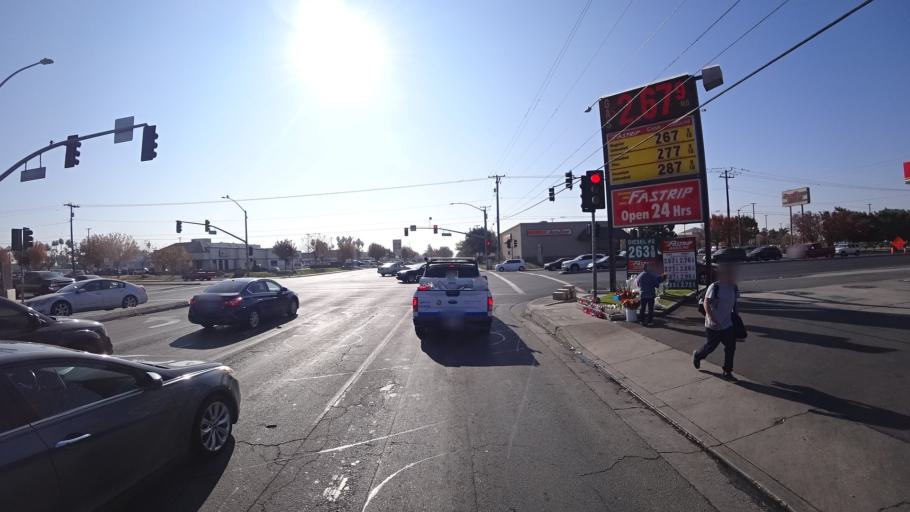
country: US
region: California
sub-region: Kern County
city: Greenfield
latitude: 35.3179
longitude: -119.0214
